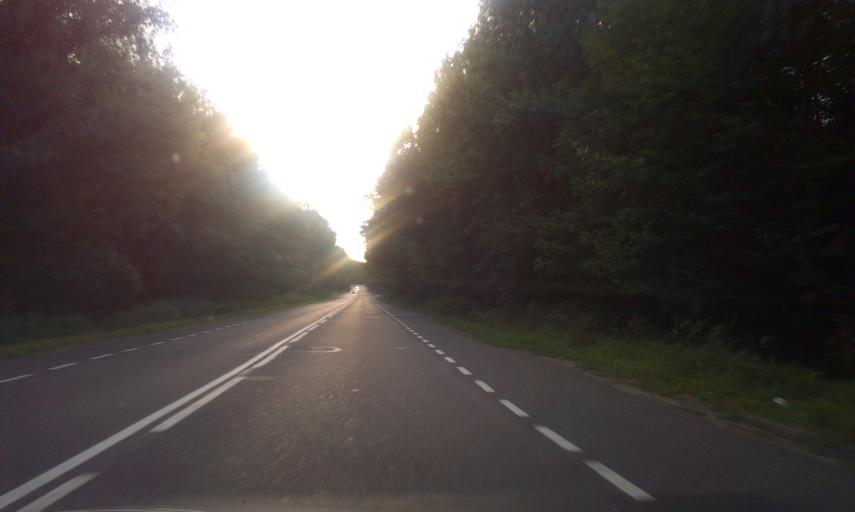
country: PL
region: West Pomeranian Voivodeship
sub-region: Powiat koszalinski
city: Sianow
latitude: 54.2223
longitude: 16.2555
